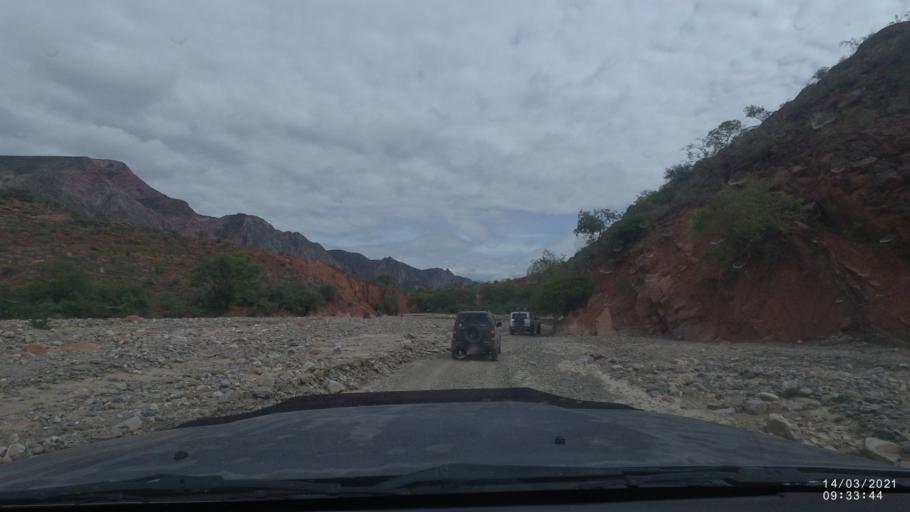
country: BO
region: Cochabamba
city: Cliza
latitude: -17.9443
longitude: -65.8586
